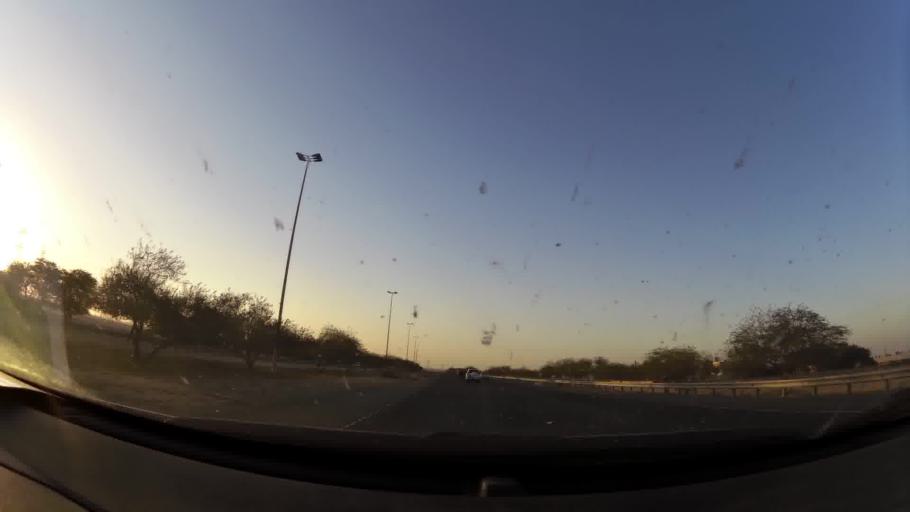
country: KW
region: Al Ahmadi
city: Al Fahahil
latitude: 28.9223
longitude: 48.2019
